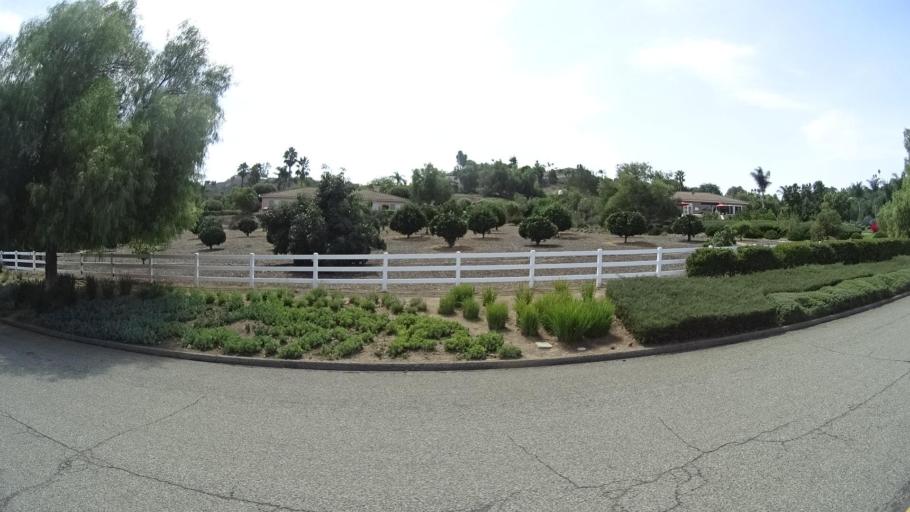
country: US
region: California
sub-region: San Diego County
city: Escondido
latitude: 33.0950
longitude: -117.0240
